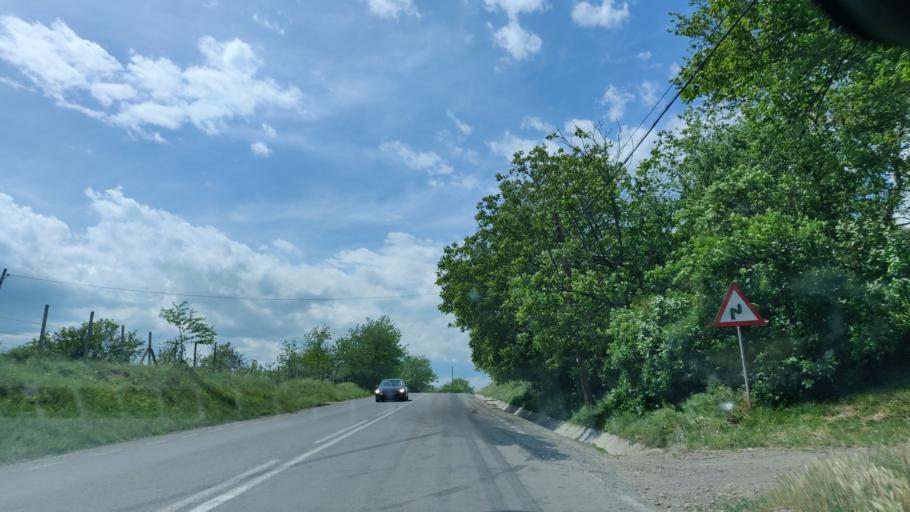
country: RO
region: Vrancea
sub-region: Comuna Vidra
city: Vidra
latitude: 45.8981
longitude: 26.8742
